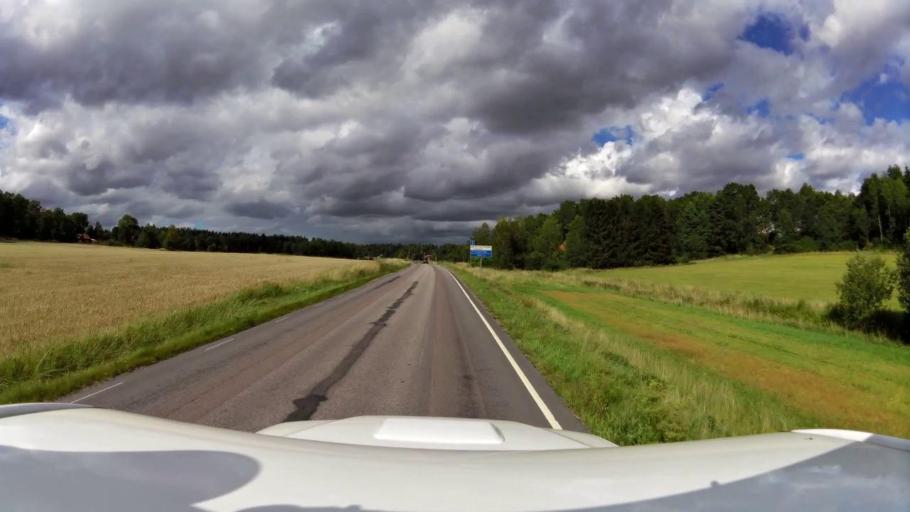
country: SE
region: OEstergoetland
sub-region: Linkopings Kommun
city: Sturefors
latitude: 58.3356
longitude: 15.7142
